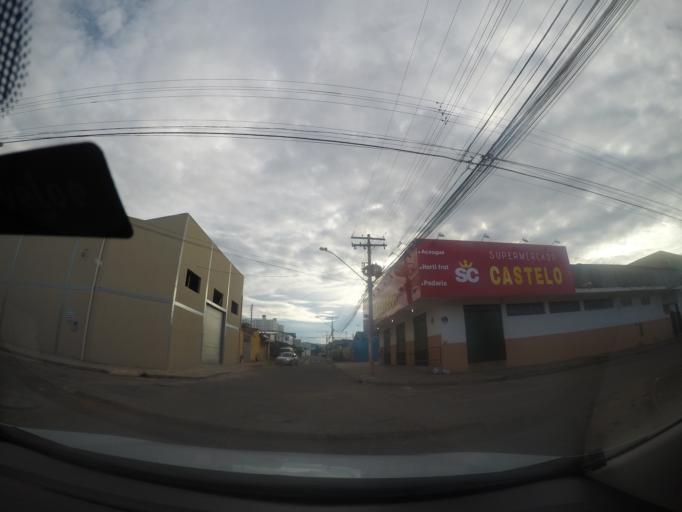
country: BR
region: Goias
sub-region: Goiania
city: Goiania
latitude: -16.6432
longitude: -49.3228
